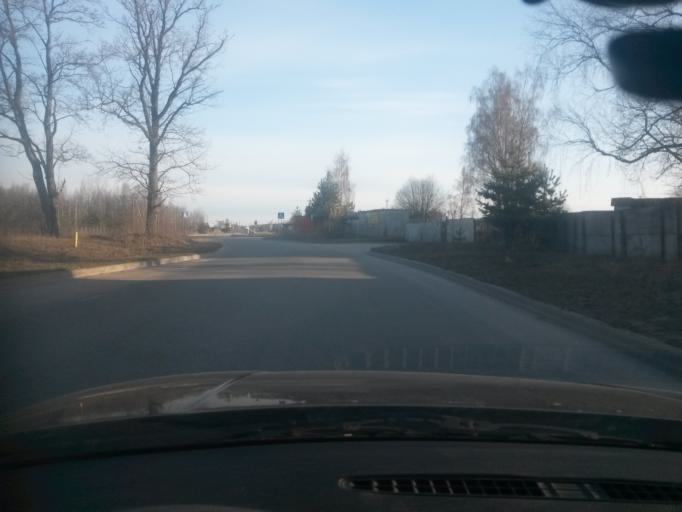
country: LV
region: Stopini
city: Ulbroka
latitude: 56.9054
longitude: 24.2466
